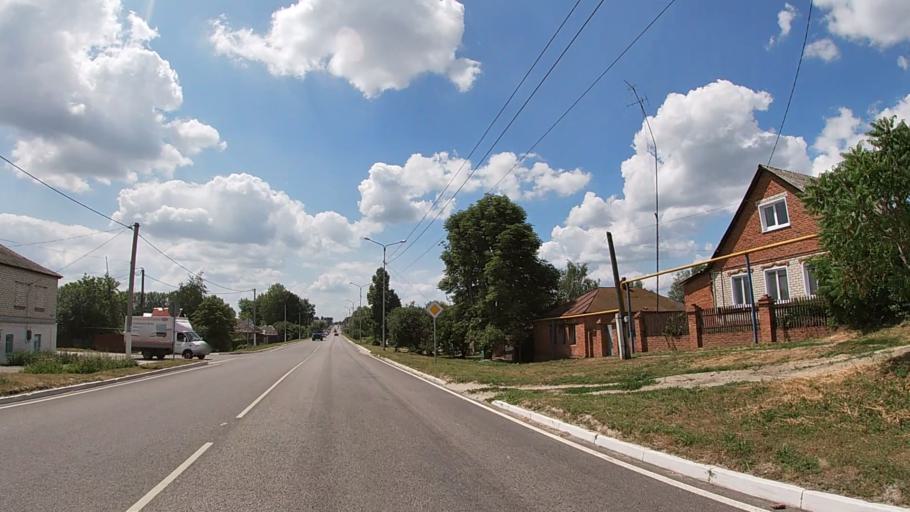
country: RU
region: Belgorod
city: Grayvoron
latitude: 50.4842
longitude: 35.6876
